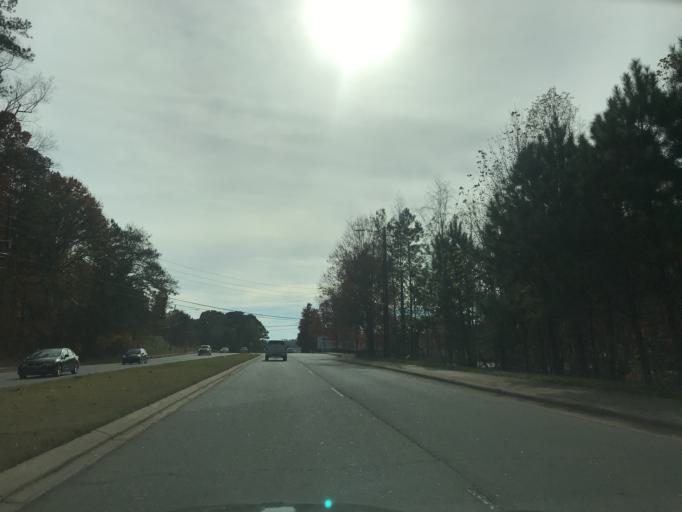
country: US
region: North Carolina
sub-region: Wake County
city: West Raleigh
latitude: 35.8472
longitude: -78.6803
